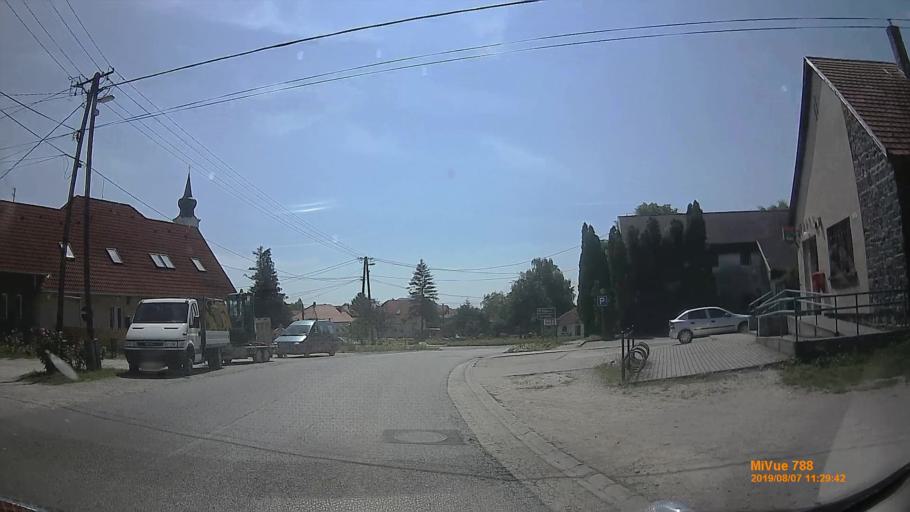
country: HU
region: Veszprem
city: Tapolca
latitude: 46.9154
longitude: 17.4577
